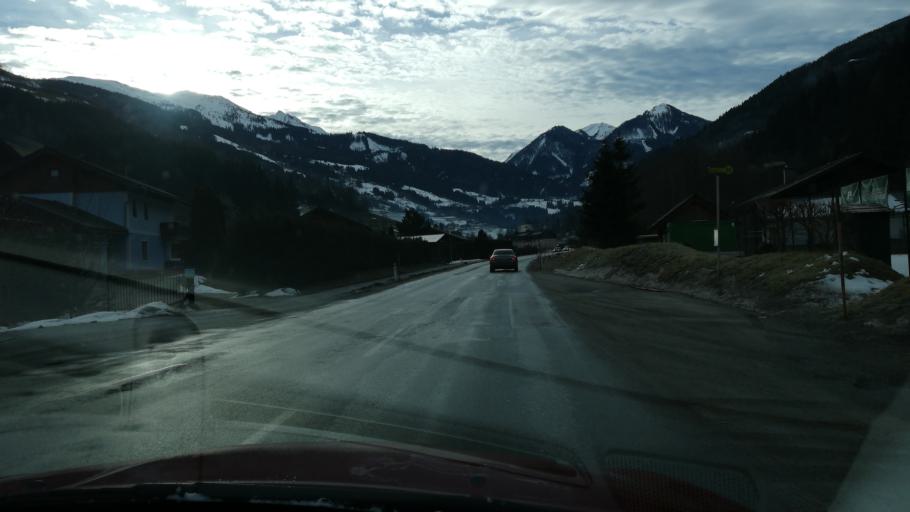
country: AT
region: Styria
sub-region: Politischer Bezirk Liezen
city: Donnersbach
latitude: 47.4733
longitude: 14.1210
